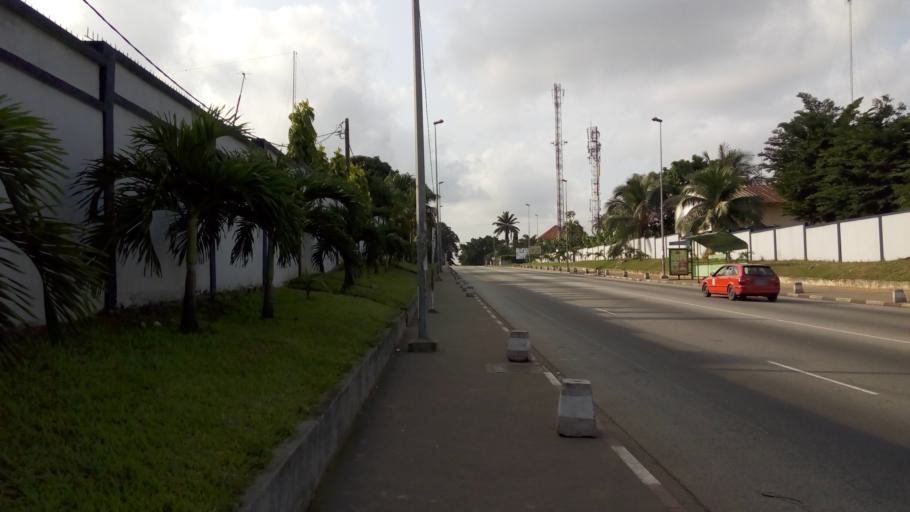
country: CI
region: Lagunes
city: Abidjan
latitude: 5.3365
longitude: -4.0218
